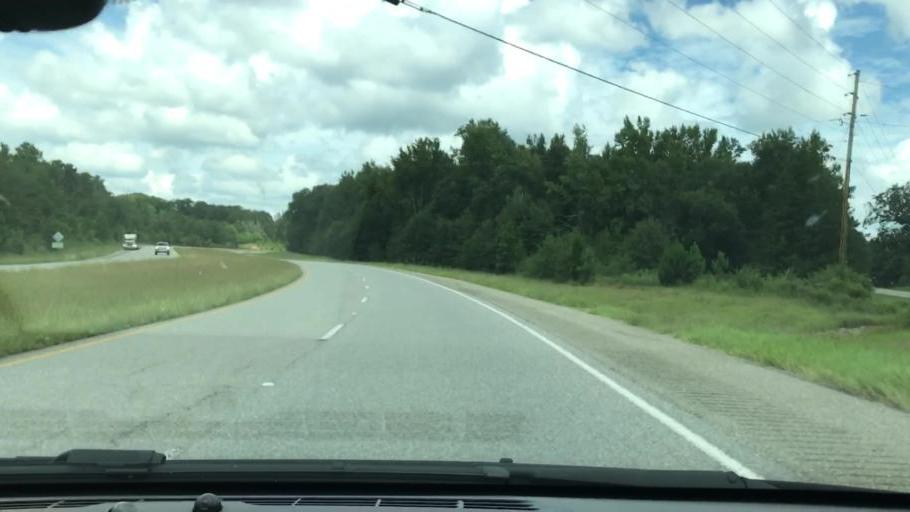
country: US
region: Georgia
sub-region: Stewart County
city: Lumpkin
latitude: 32.1575
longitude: -84.8290
